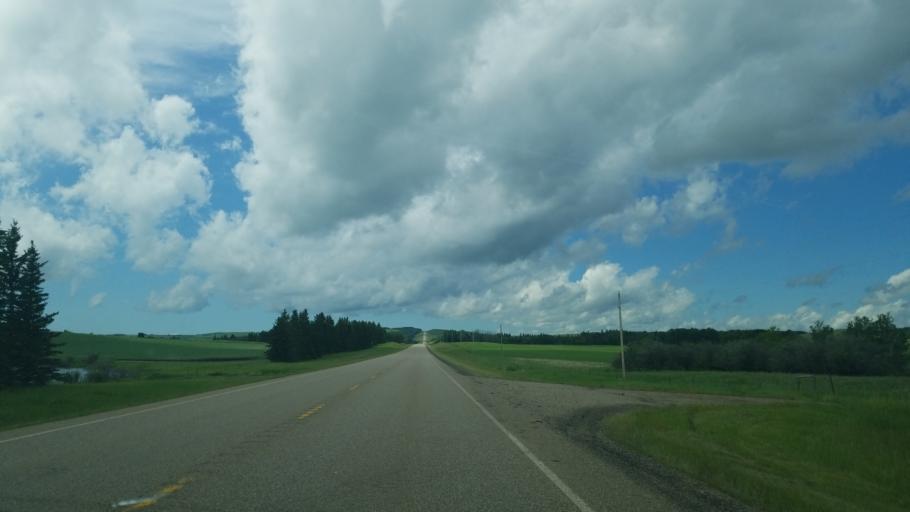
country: CA
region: Saskatchewan
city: Lloydminster
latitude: 53.1616
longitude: -110.1879
